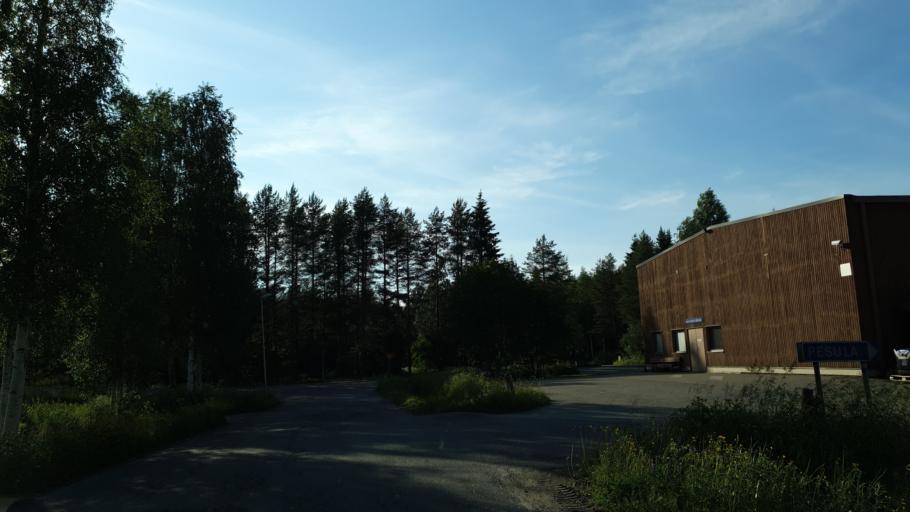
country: FI
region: Kainuu
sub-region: Kehys-Kainuu
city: Kuhmo
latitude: 64.1231
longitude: 29.5033
